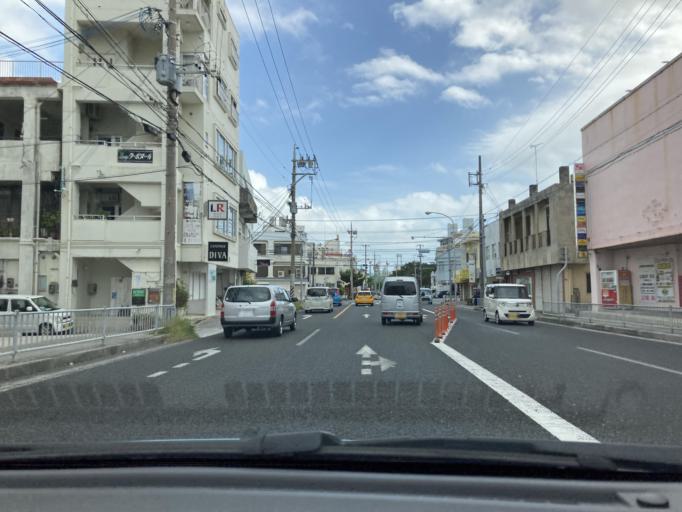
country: JP
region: Okinawa
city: Ginowan
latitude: 26.2600
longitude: 127.7436
